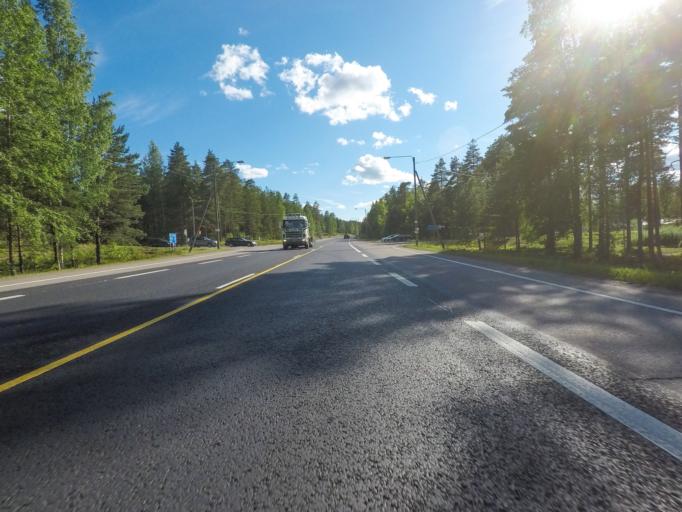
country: FI
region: Uusimaa
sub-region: Helsinki
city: Vihti
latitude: 60.3431
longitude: 24.3077
